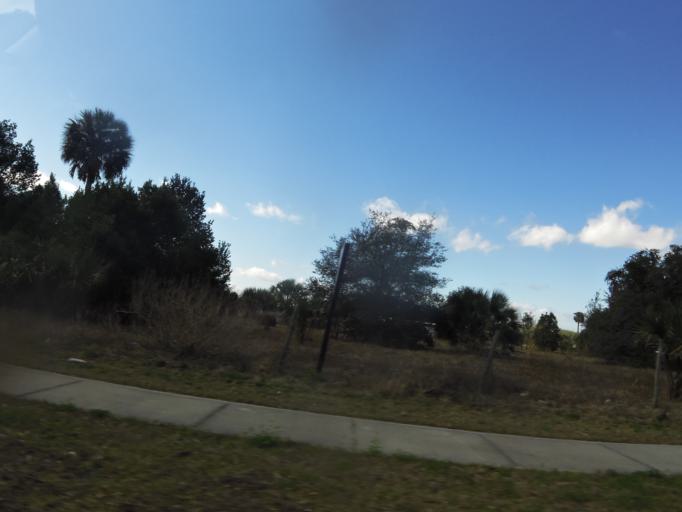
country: US
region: Florida
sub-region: Volusia County
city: Pierson
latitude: 29.2383
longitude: -81.4629
